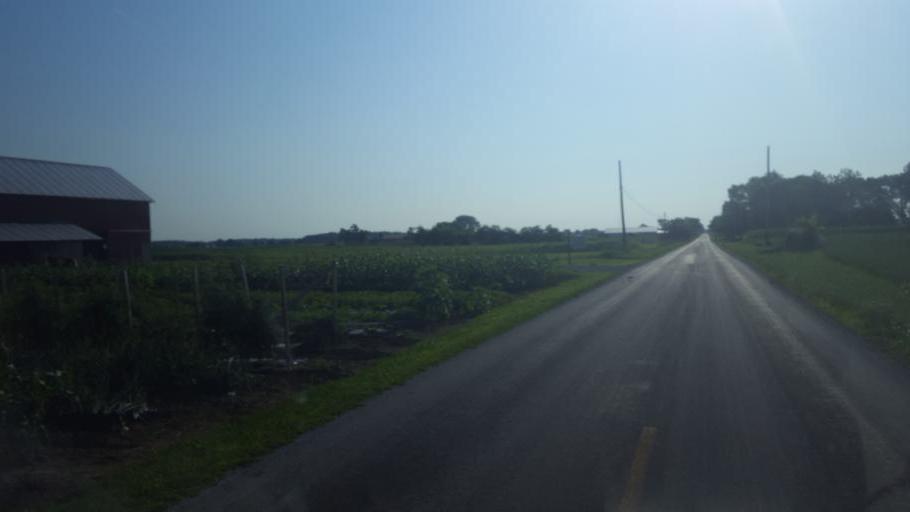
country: US
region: Ohio
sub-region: Hardin County
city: Kenton
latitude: 40.5631
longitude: -83.5389
